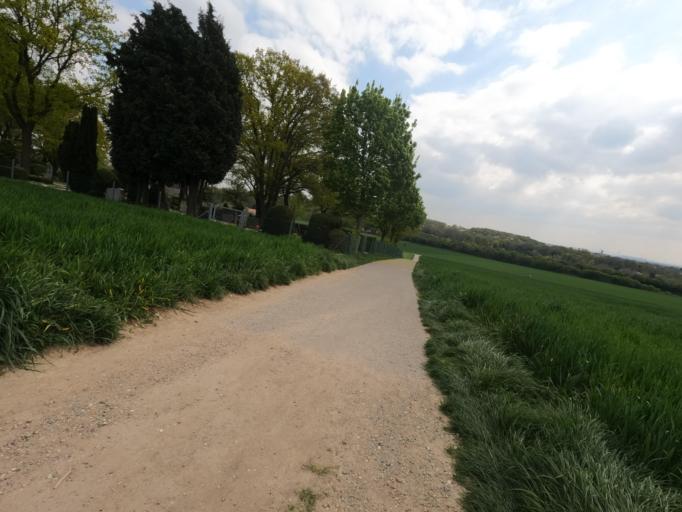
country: DE
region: North Rhine-Westphalia
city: Huckelhoven
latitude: 51.0730
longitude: 6.2190
